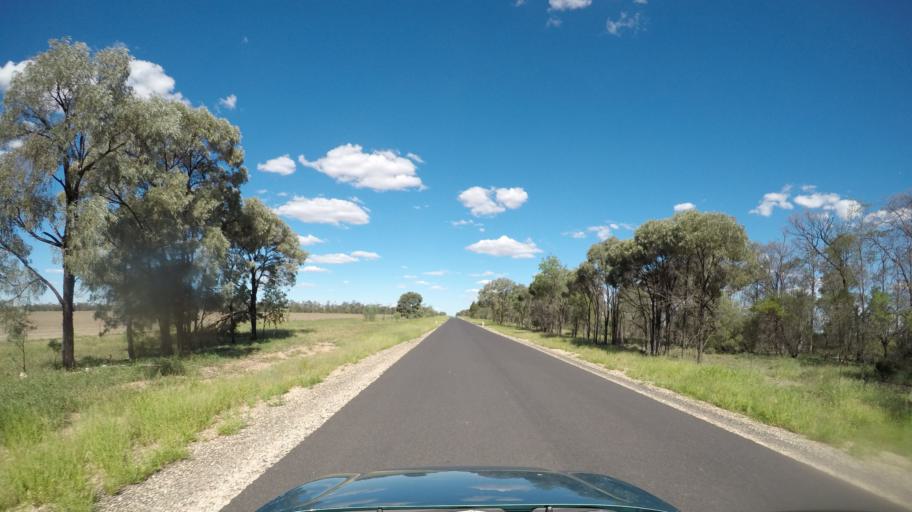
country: AU
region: Queensland
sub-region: Goondiwindi
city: Goondiwindi
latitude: -28.1664
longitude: 150.1810
